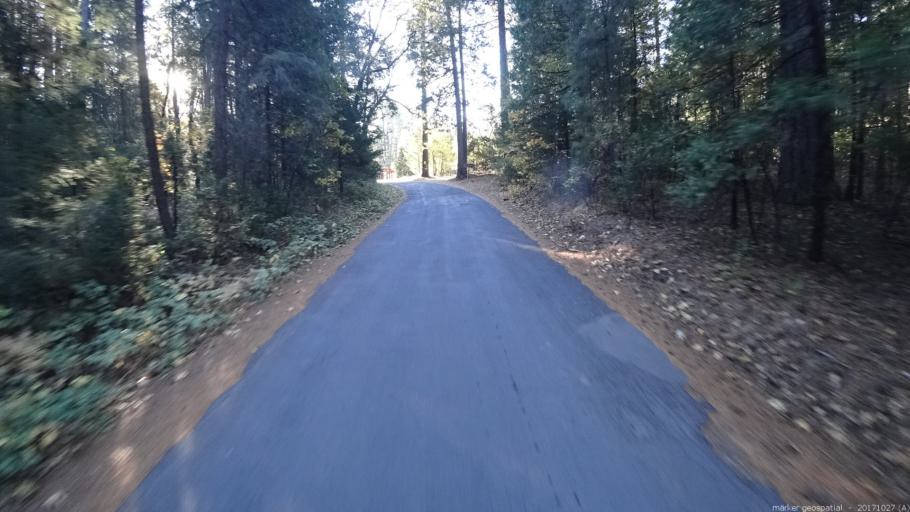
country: US
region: California
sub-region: Shasta County
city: Burney
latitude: 41.0036
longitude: -121.8915
